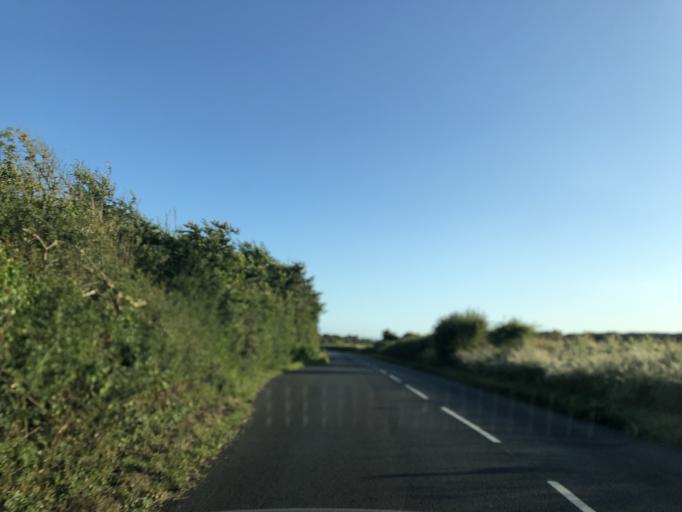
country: GB
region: England
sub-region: Isle of Wight
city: Shalfleet
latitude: 50.6392
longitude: -1.4028
